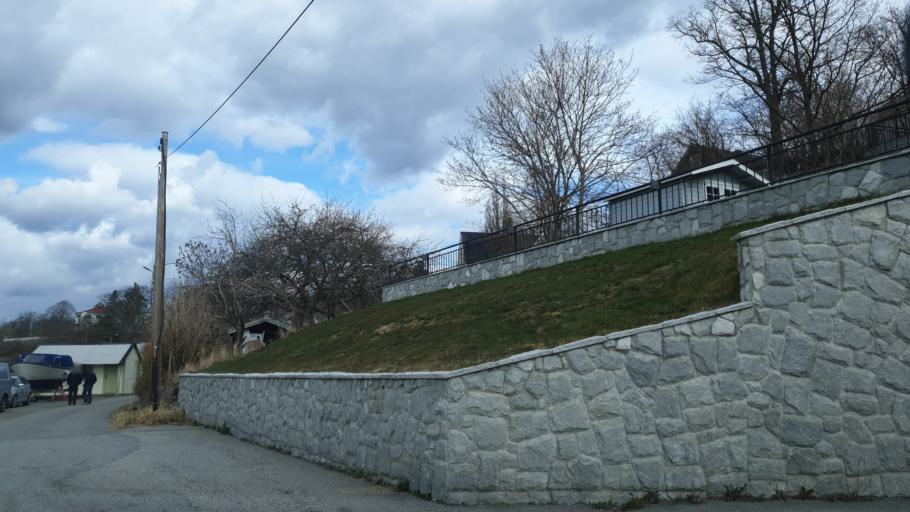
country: SE
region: Stockholm
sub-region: Lidingo
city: Brevik
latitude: 59.3096
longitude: 18.2218
